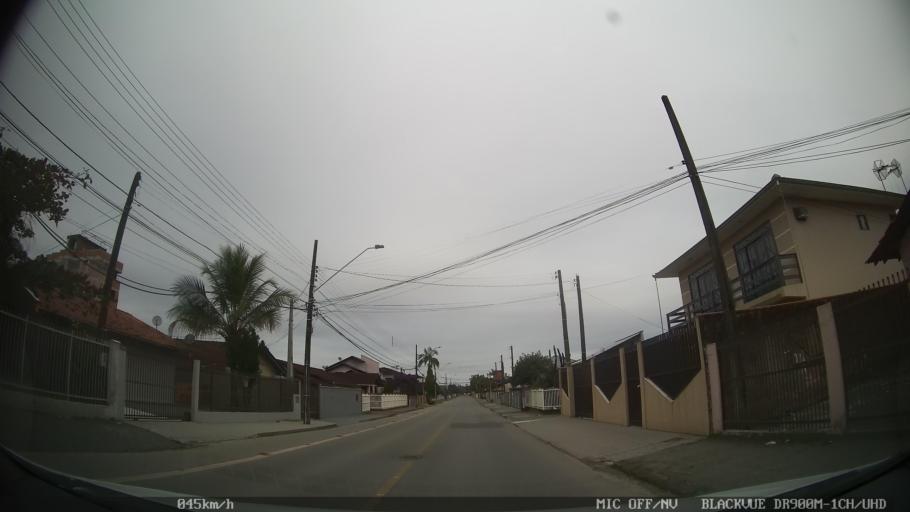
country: BR
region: Santa Catarina
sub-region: Joinville
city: Joinville
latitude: -26.2897
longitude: -48.9100
